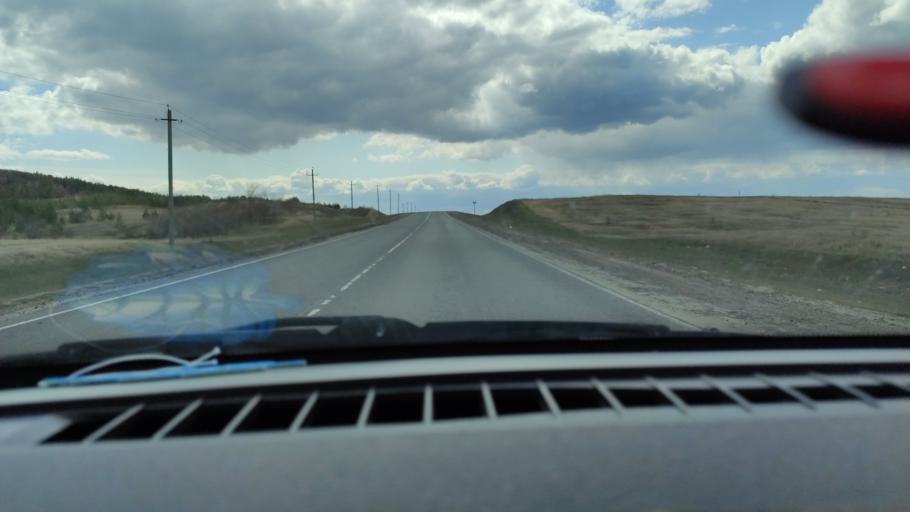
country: RU
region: Saratov
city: Alekseyevka
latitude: 52.2993
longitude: 47.9275
